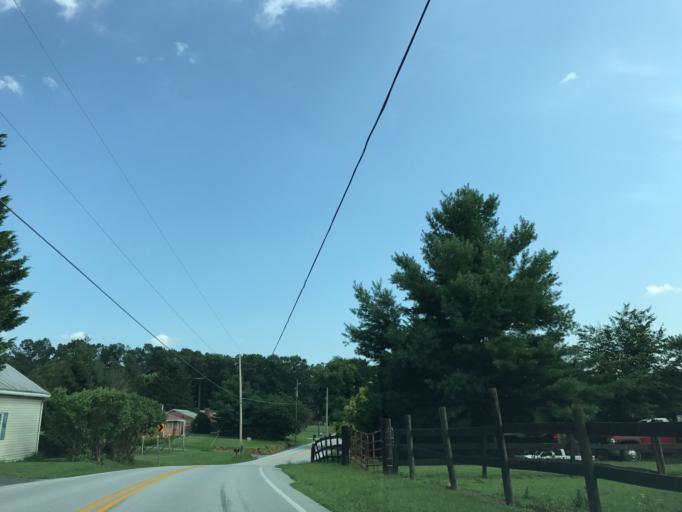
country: US
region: Pennsylvania
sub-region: York County
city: Pennville
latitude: 39.7495
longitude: -77.0250
